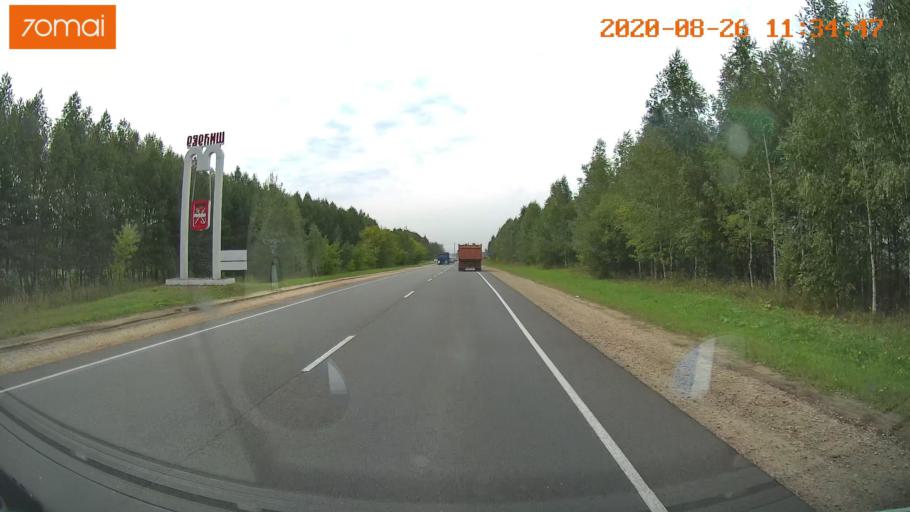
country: RU
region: Rjazan
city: Shilovo
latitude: 54.2812
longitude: 40.8399
